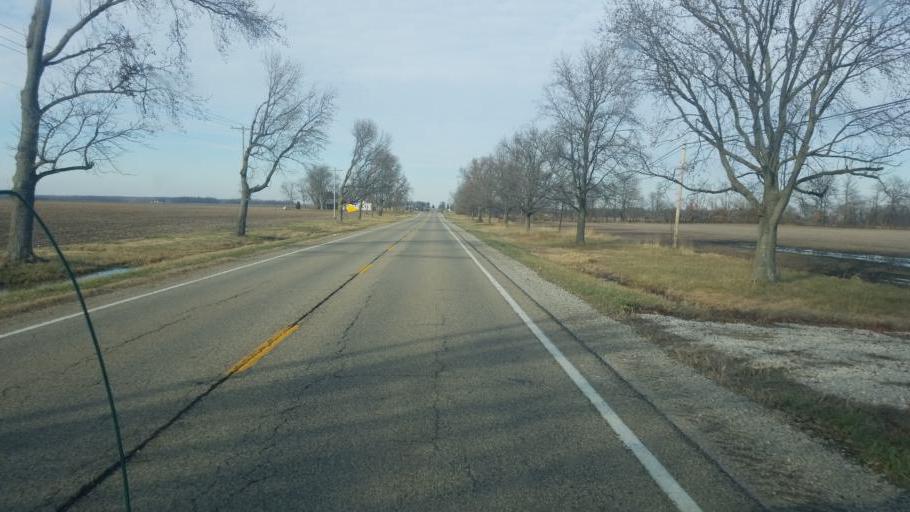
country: US
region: Illinois
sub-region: Lawrence County
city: Bridgeport
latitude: 38.5951
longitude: -87.6943
